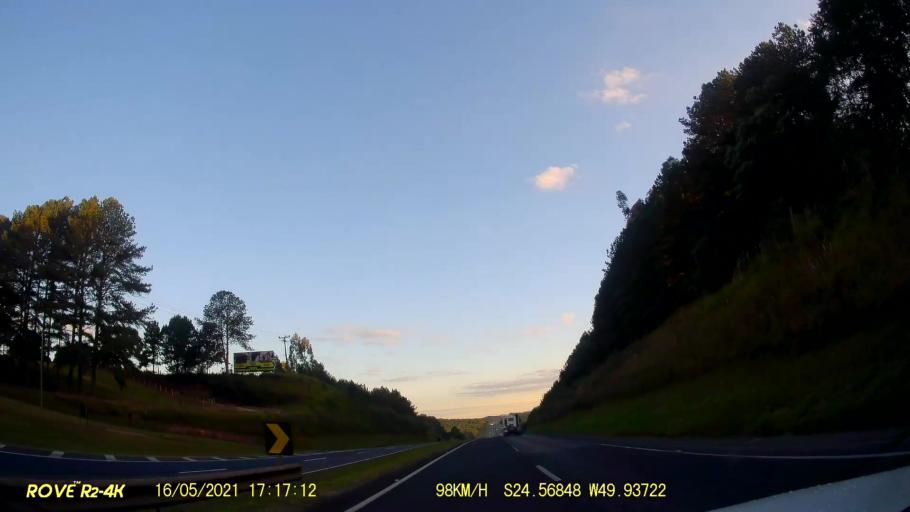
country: BR
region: Parana
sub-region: Pirai Do Sul
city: Pirai do Sul
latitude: -24.5689
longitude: -49.9373
